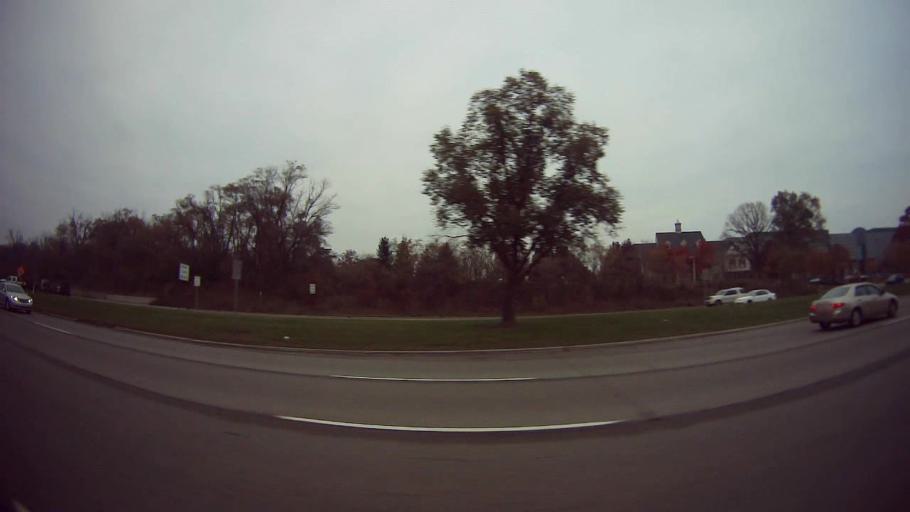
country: US
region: Michigan
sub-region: Oakland County
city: Bingham Farms
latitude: 42.4756
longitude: -83.2844
